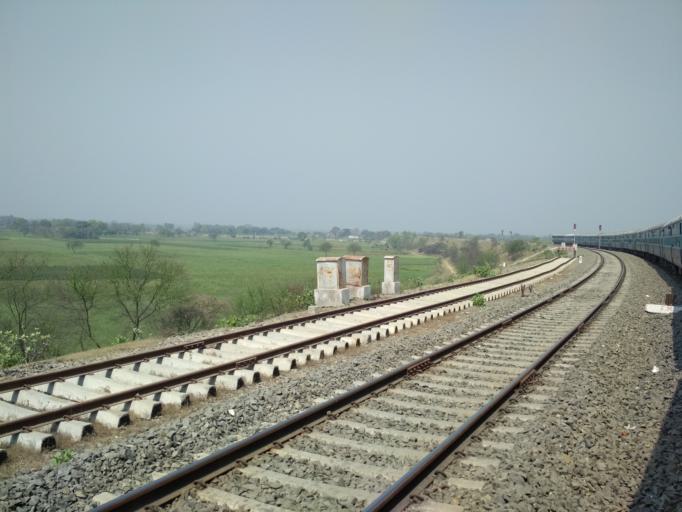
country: IN
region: Bihar
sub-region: Munger
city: Munger
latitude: 25.4328
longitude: 86.4386
